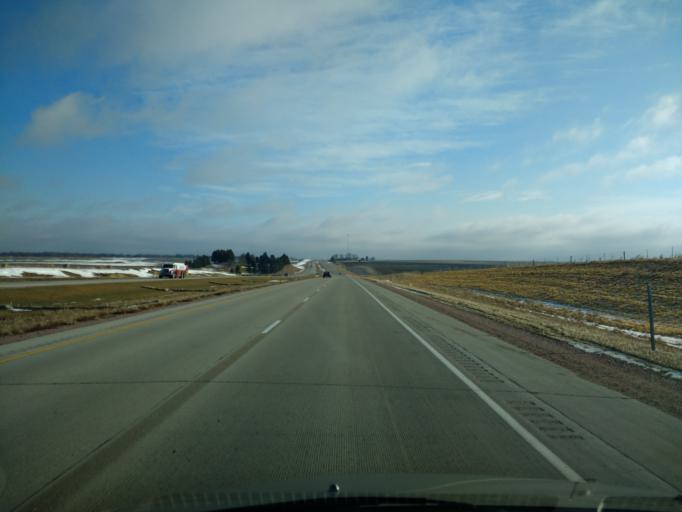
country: US
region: Iowa
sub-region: Ida County
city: Holstein
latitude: 42.4743
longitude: -95.5704
